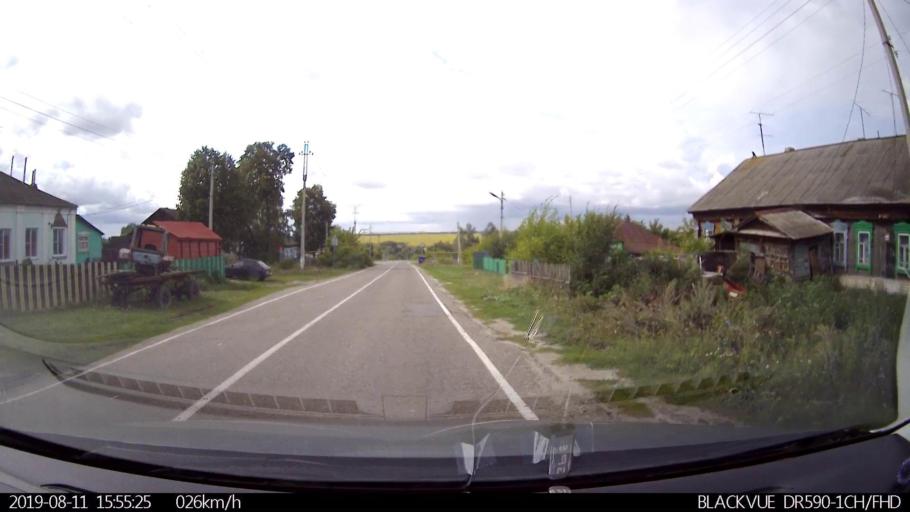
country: RU
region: Ulyanovsk
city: Ignatovka
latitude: 53.9452
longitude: 47.6543
